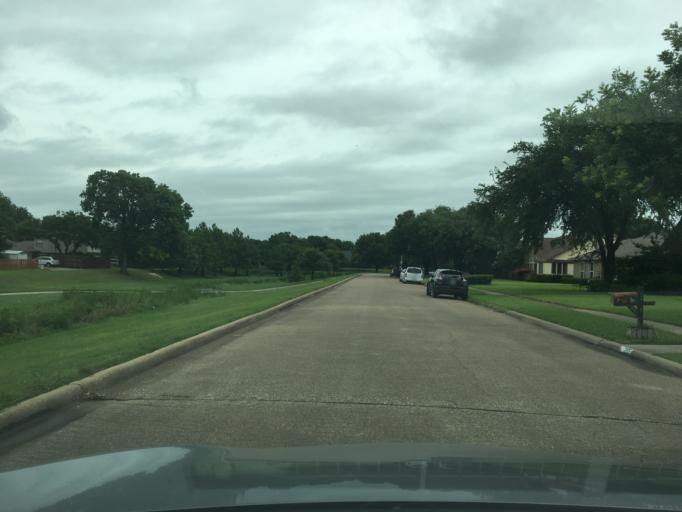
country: US
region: Texas
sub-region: Dallas County
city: Richardson
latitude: 32.9496
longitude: -96.6899
